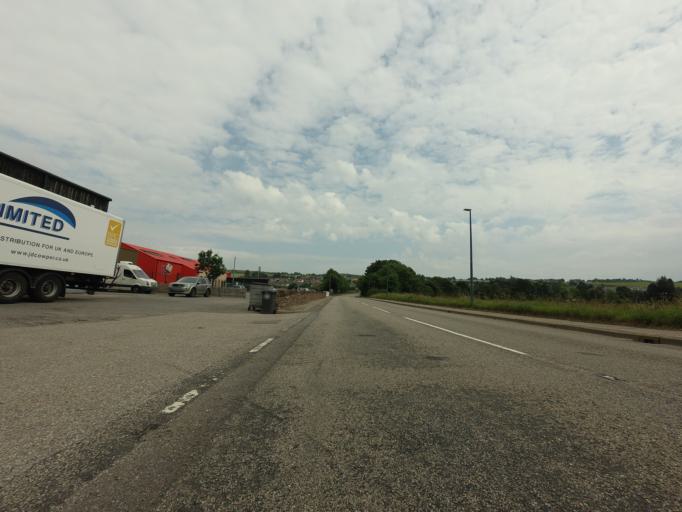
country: GB
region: Scotland
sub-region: Highland
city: Alness
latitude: 57.8902
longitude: -4.3520
